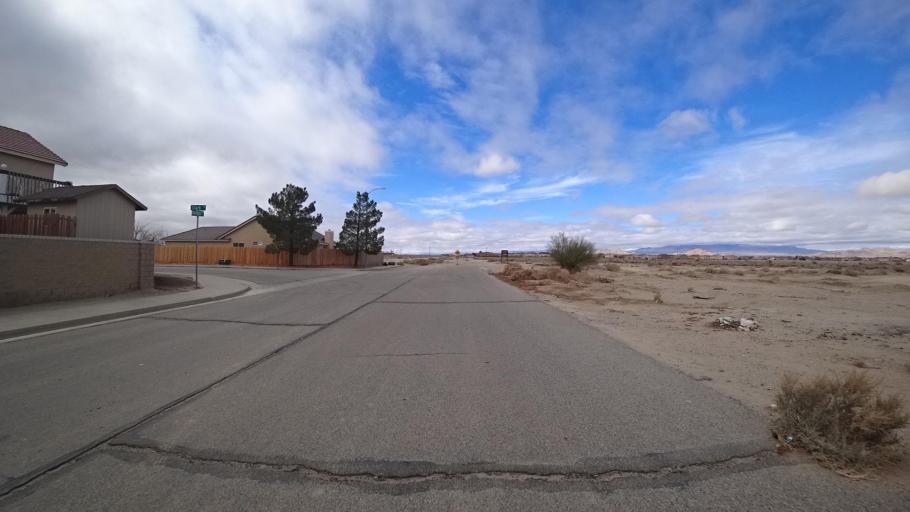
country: US
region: California
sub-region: Kern County
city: Rosamond
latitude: 34.8495
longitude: -118.1800
